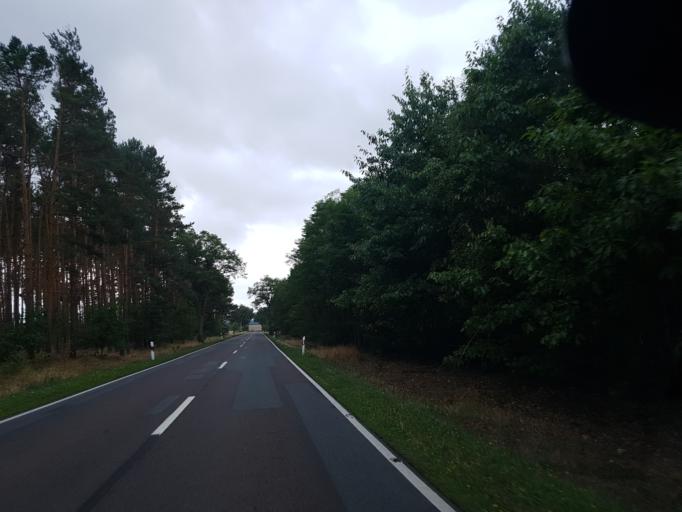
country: DE
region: Saxony-Anhalt
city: Loburg
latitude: 52.1384
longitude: 12.0912
